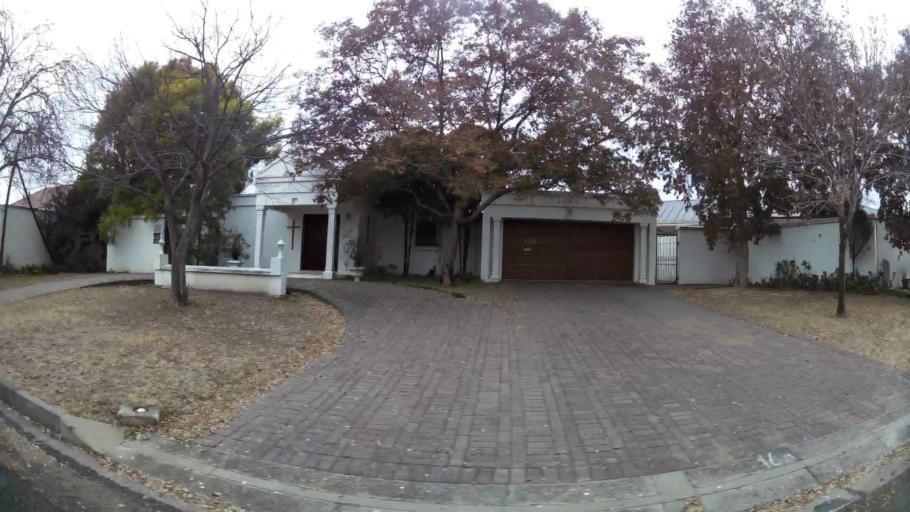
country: ZA
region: Orange Free State
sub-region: Fezile Dabi District Municipality
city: Kroonstad
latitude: -27.6776
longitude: 27.2436
